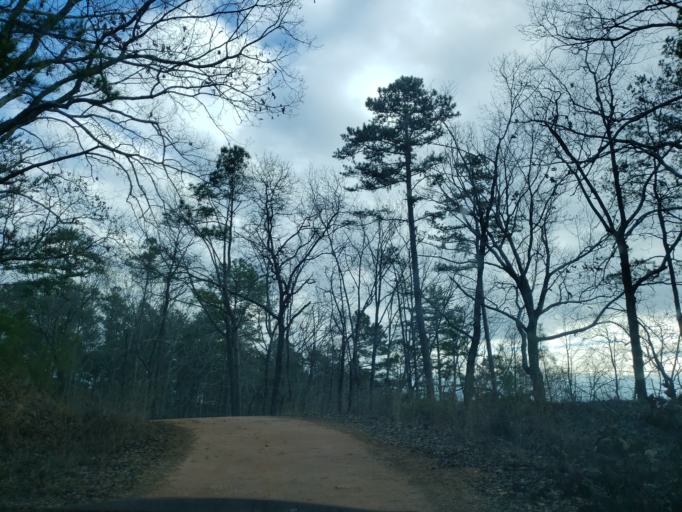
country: US
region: Alabama
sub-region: Cleburne County
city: Heflin
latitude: 33.6908
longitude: -85.6362
